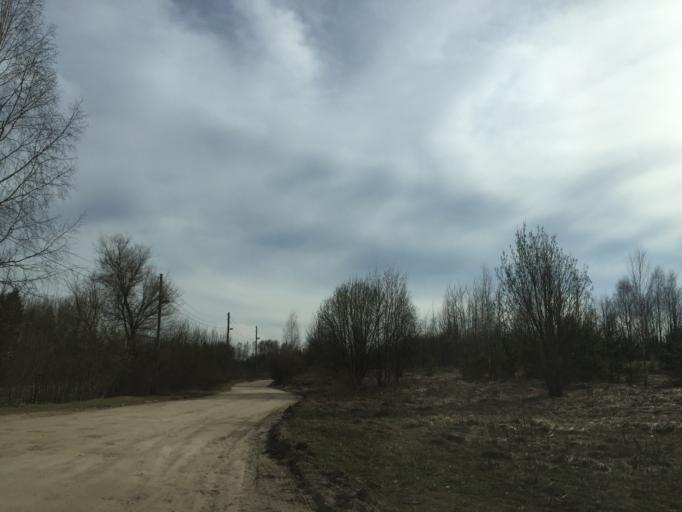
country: LV
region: Ogre
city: Ogre
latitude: 56.8088
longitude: 24.6473
